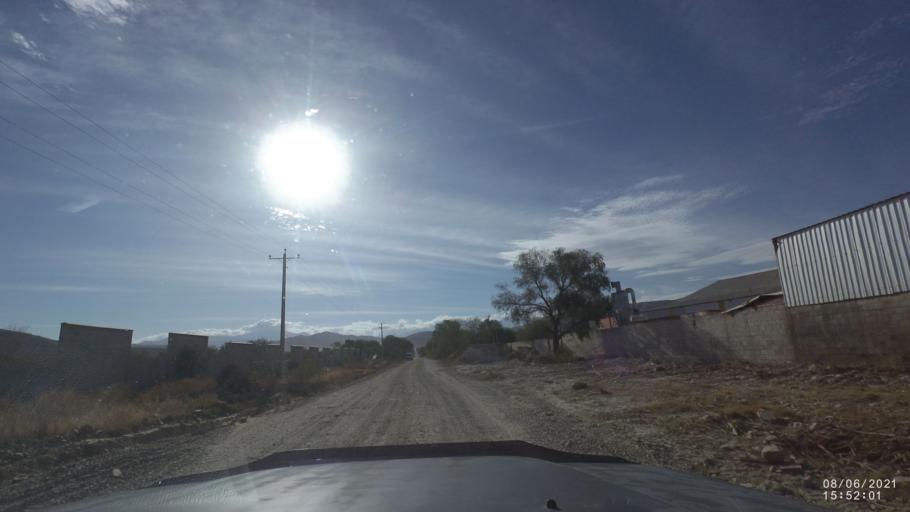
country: BO
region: Cochabamba
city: Capinota
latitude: -17.5584
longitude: -66.2529
